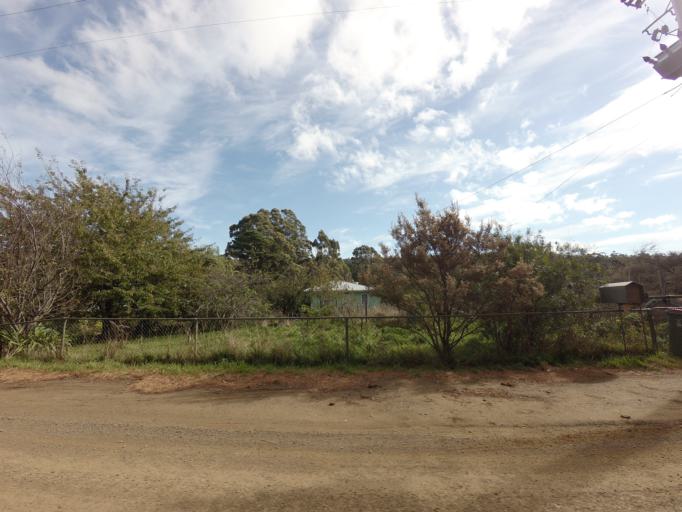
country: AU
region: Tasmania
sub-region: Clarence
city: Sandford
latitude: -43.1470
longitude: 147.7644
